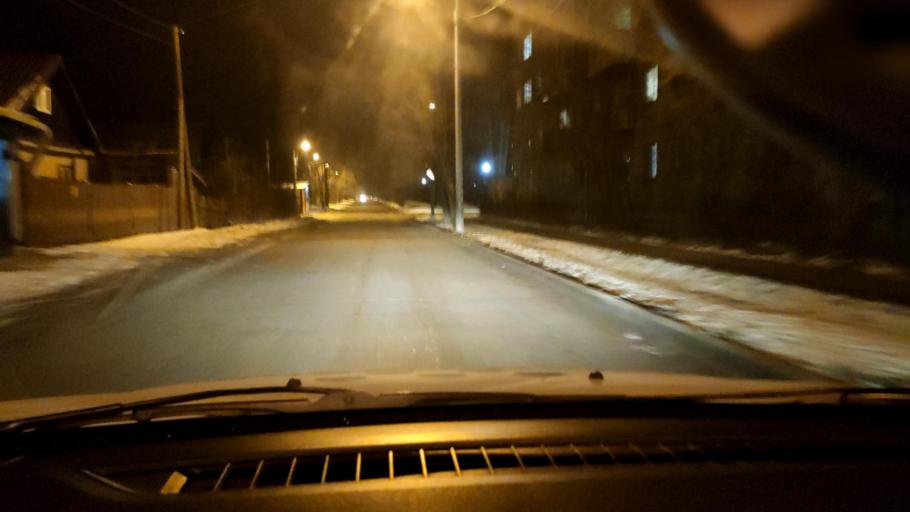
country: RU
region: Perm
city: Overyata
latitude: 58.0300
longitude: 55.8423
